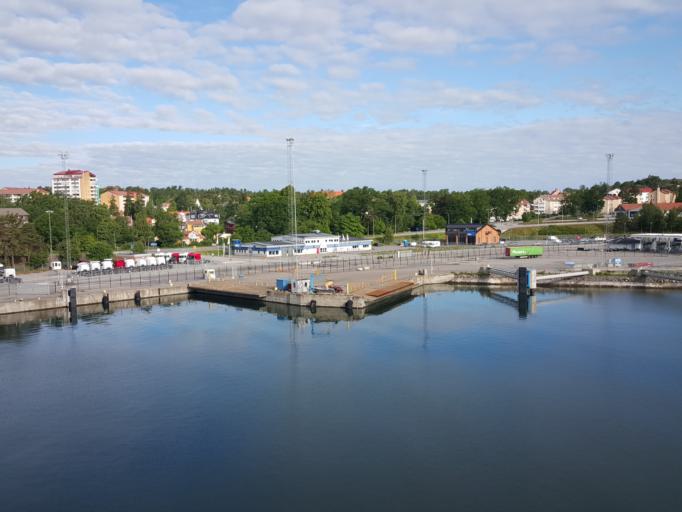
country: SE
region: Stockholm
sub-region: Nynashamns Kommun
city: Nynashamn
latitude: 58.9062
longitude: 17.9590
